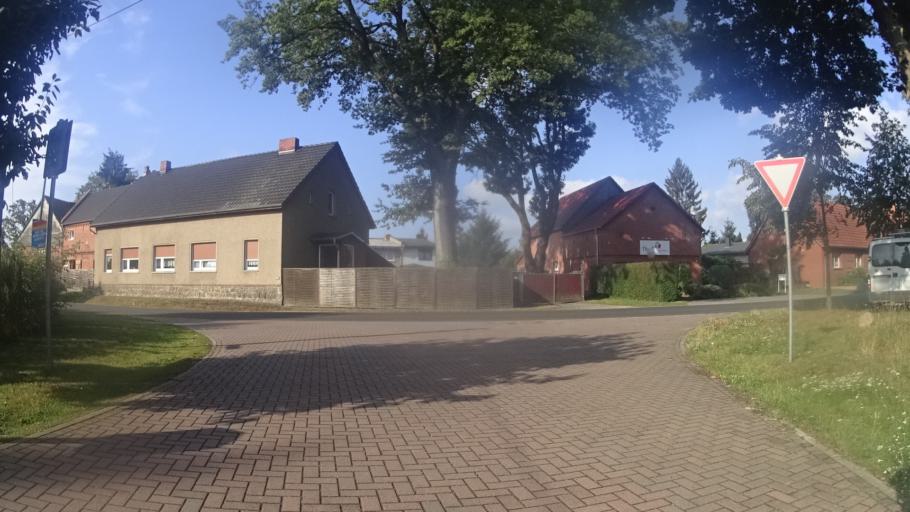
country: DE
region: Brandenburg
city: Cumlosen
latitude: 53.0308
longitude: 11.6587
